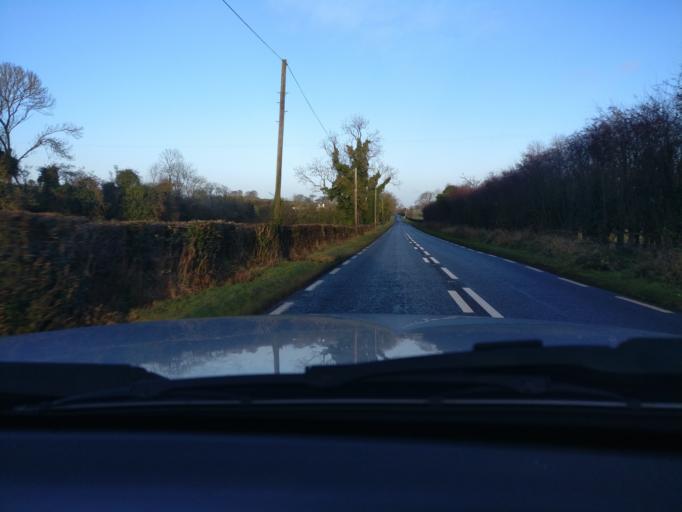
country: IE
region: Leinster
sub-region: Lu
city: Ardee
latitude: 53.8026
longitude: -6.6740
